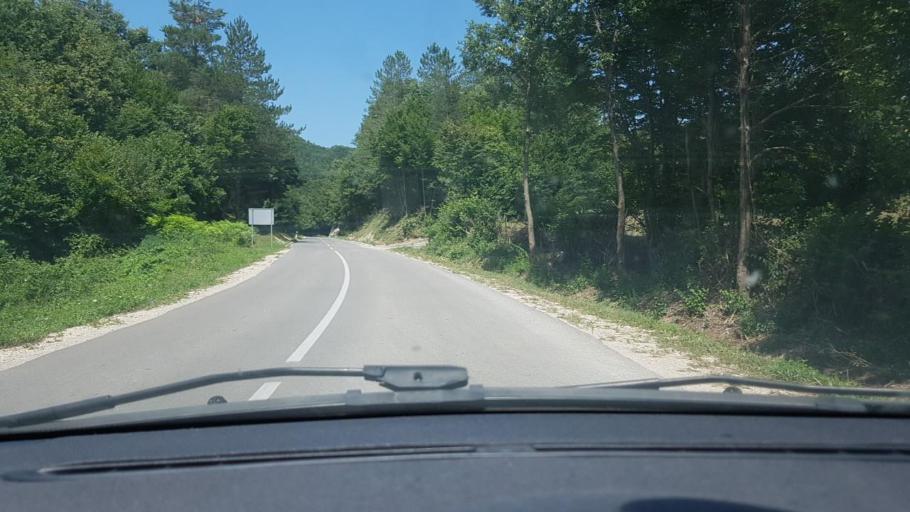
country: BA
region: Federation of Bosnia and Herzegovina
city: Orasac
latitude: 44.6111
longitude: 16.0713
